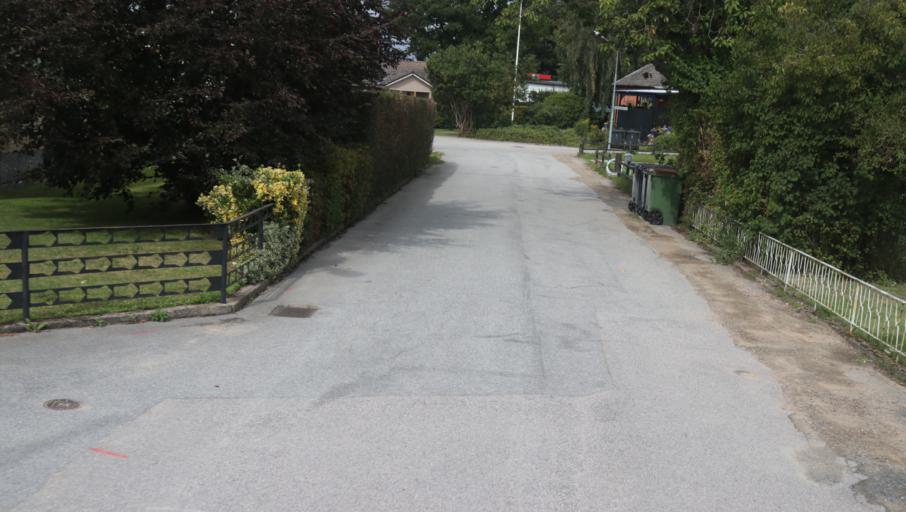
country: SE
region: Blekinge
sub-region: Karlshamns Kommun
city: Karlshamn
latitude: 56.2114
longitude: 14.8367
